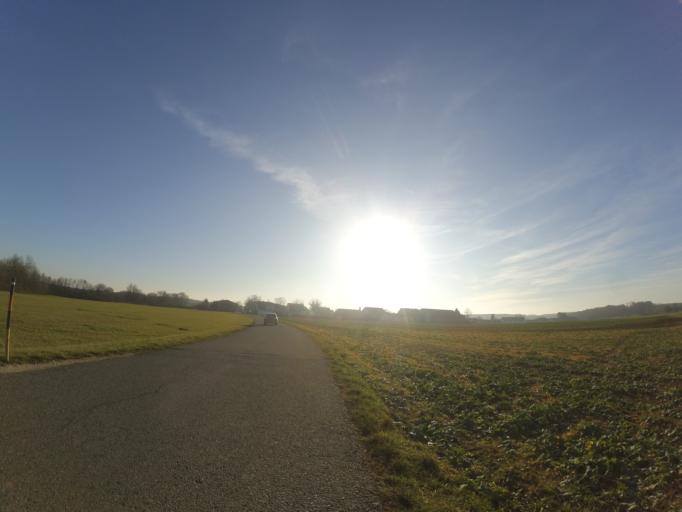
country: DE
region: Baden-Wuerttemberg
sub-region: Tuebingen Region
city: Dornstadt
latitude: 48.4481
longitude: 9.8963
